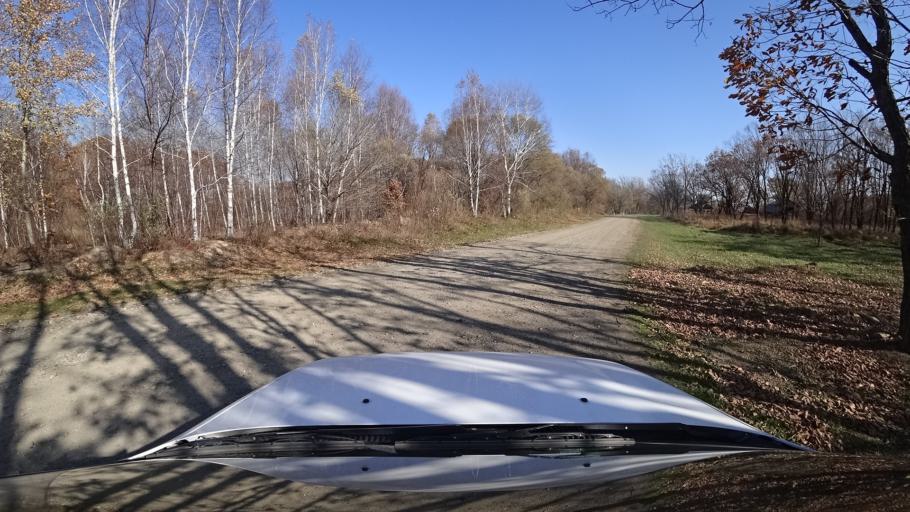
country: RU
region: Primorskiy
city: Dal'nerechensk
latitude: 45.8828
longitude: 133.7231
